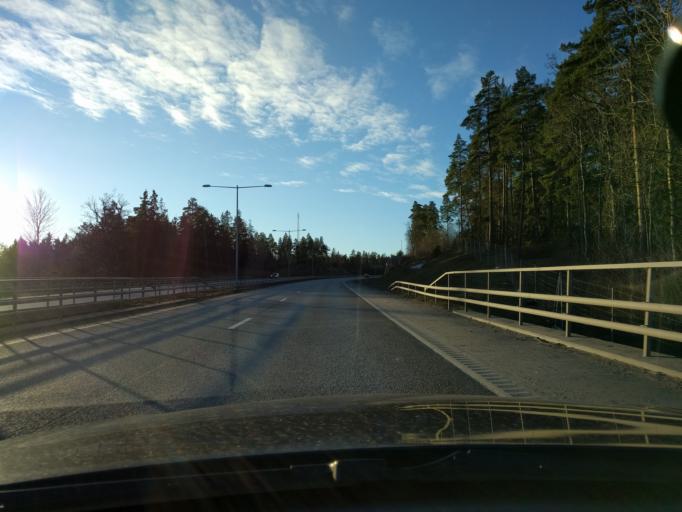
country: SE
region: Stockholm
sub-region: Sollentuna Kommun
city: Sollentuna
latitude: 59.4701
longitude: 17.9835
